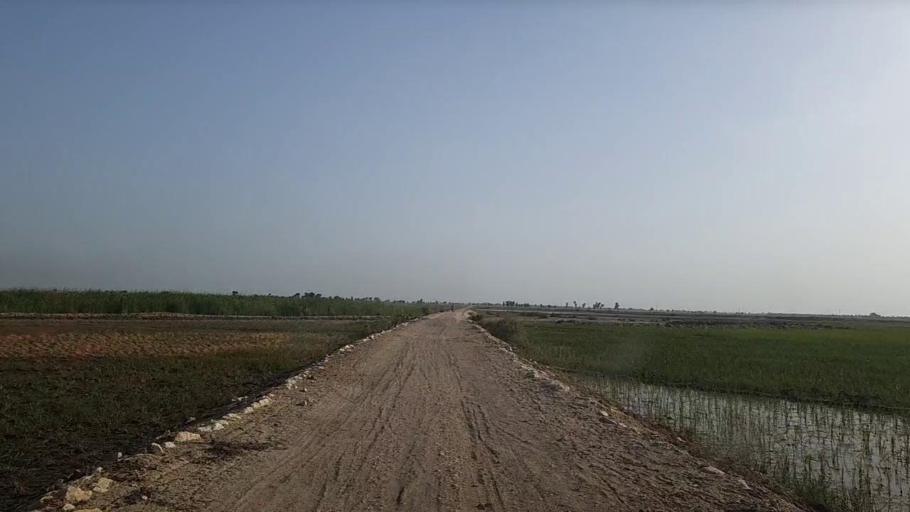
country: PK
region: Sindh
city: Sita Road
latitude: 27.1078
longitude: 67.8904
